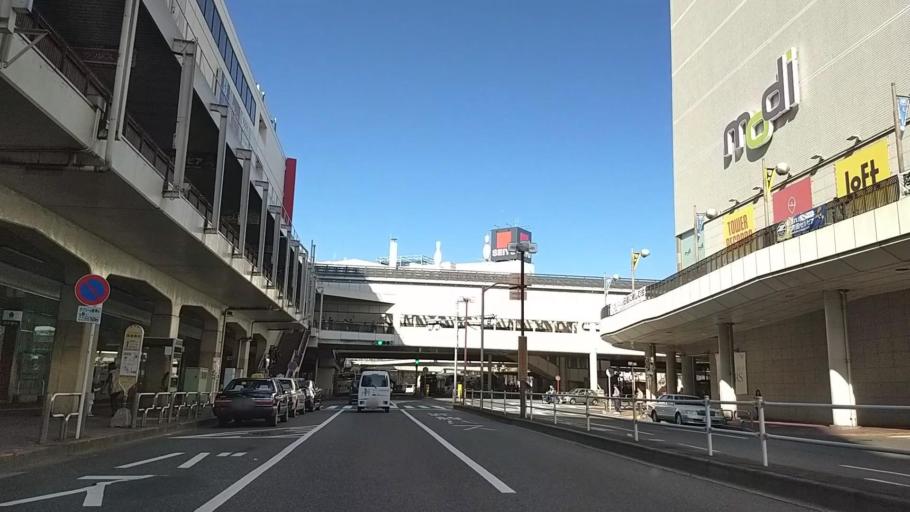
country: JP
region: Tokyo
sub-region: Machida-shi
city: Machida
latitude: 35.5427
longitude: 139.4452
